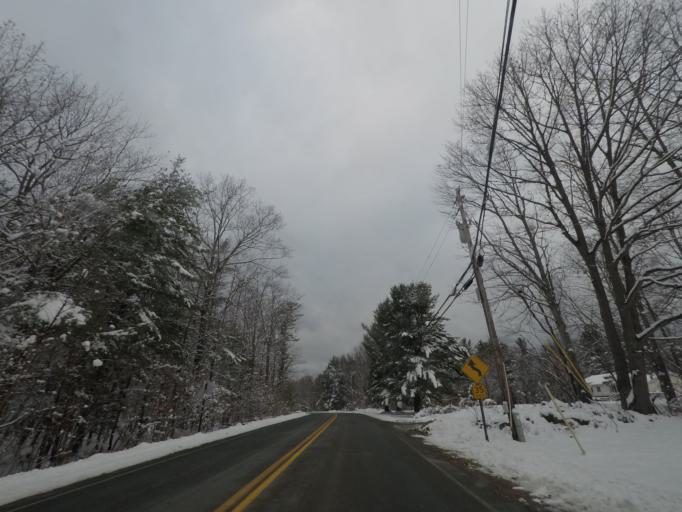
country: US
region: New York
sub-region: Rensselaer County
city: Averill Park
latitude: 42.6674
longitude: -73.5213
